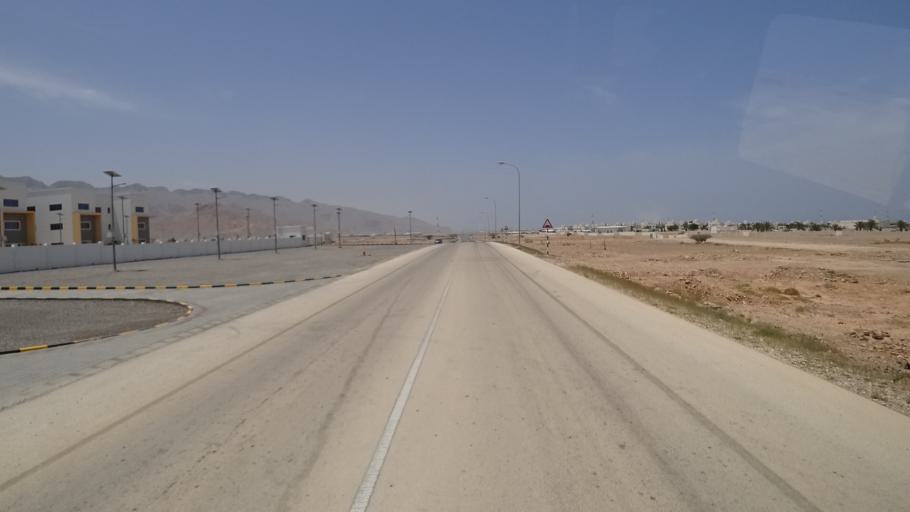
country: OM
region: Ash Sharqiyah
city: Sur
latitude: 22.6010
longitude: 59.4385
